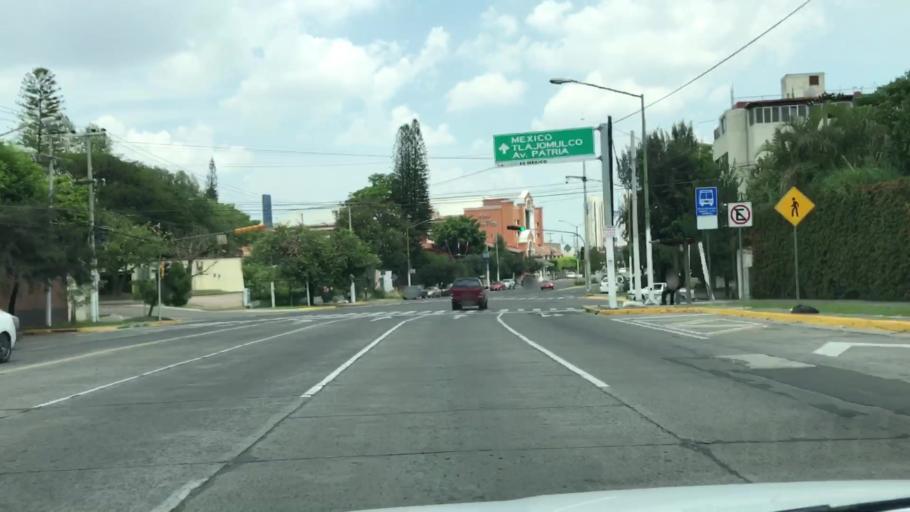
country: MX
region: Jalisco
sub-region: Zapopan
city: Zapopan
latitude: 20.7144
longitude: -103.3857
